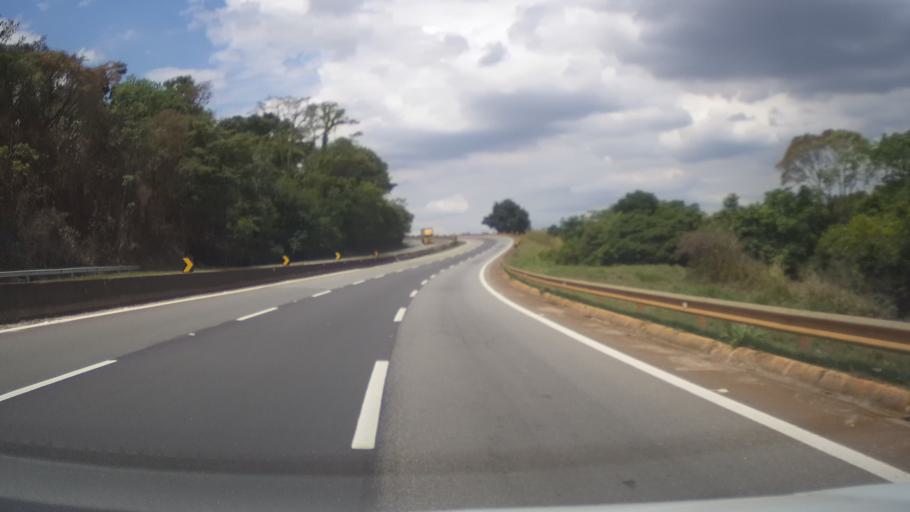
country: BR
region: Minas Gerais
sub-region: Nepomuceno
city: Nepomuceno
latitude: -21.2876
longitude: -45.1445
